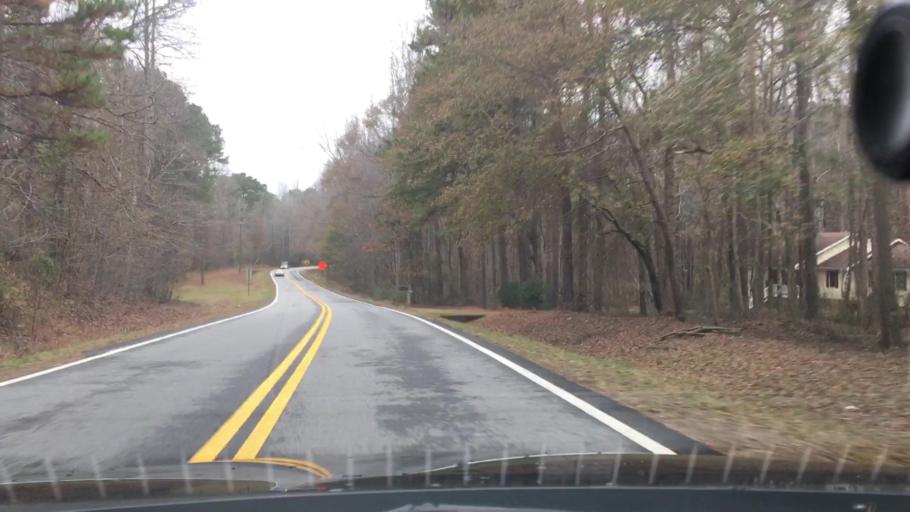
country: US
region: Georgia
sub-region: Coweta County
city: East Newnan
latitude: 33.4188
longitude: -84.7025
